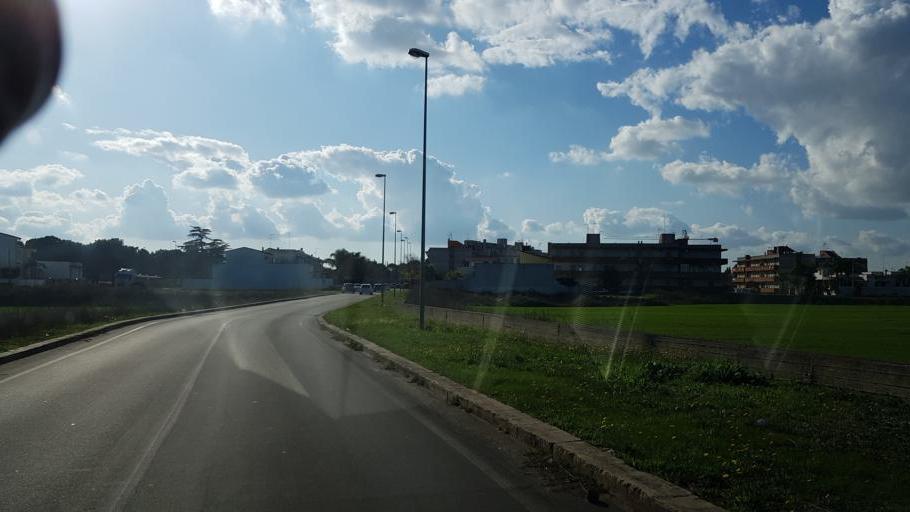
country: IT
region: Apulia
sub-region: Provincia di Lecce
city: Campi Salentina
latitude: 40.4054
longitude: 18.0178
